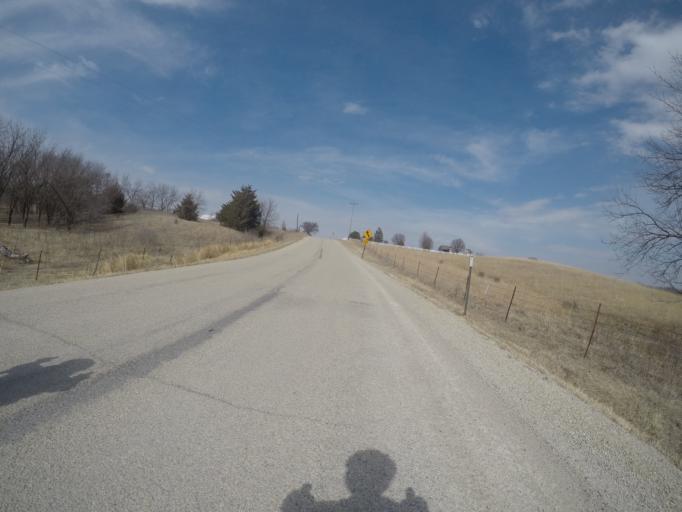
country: US
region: Kansas
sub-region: Geary County
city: Grandview Plaza
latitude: 39.0129
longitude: -96.7455
